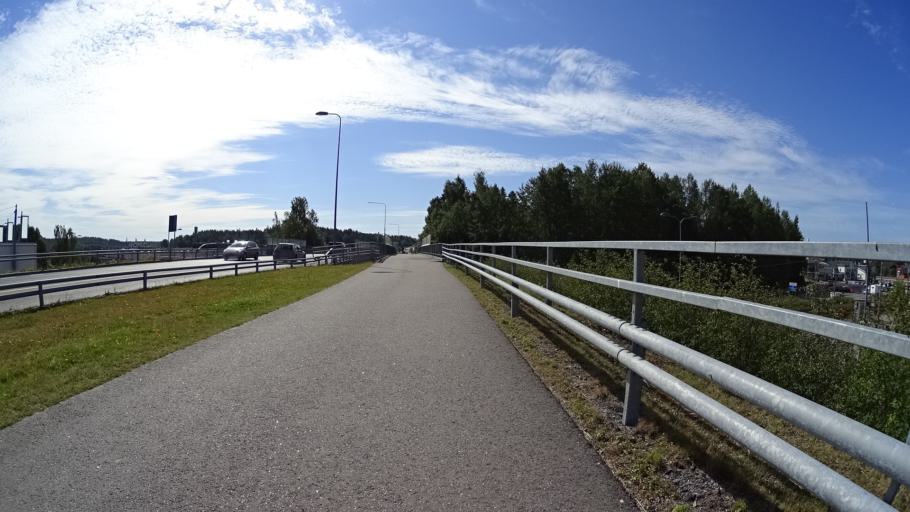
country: FI
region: Uusimaa
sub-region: Helsinki
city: Kirkkonummi
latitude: 60.1200
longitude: 24.4425
